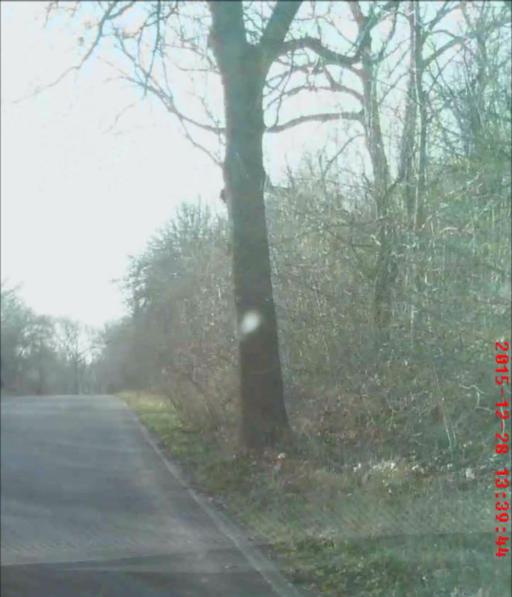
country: DE
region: Thuringia
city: Eberstedt
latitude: 51.0784
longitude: 11.5952
